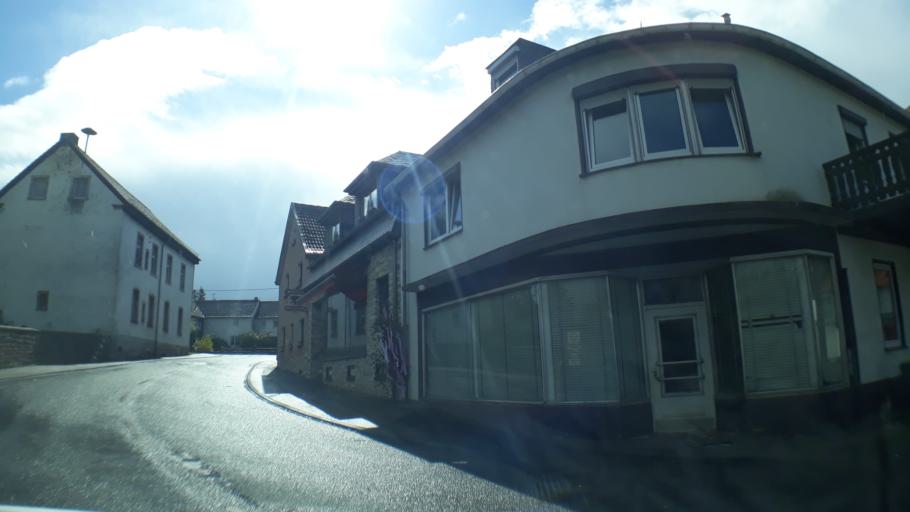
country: DE
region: North Rhine-Westphalia
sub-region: Regierungsbezirk Koln
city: Schleiden
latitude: 50.4920
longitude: 6.5179
